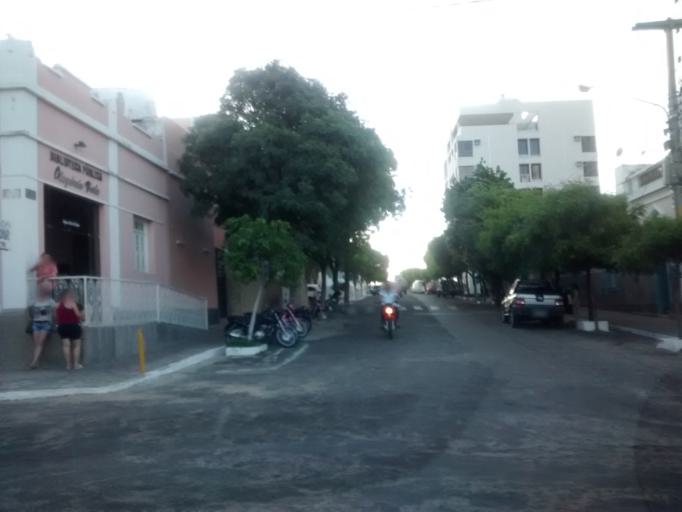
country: BR
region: Rio Grande do Norte
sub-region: Caico
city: Caico
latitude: -6.4590
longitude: -37.0946
